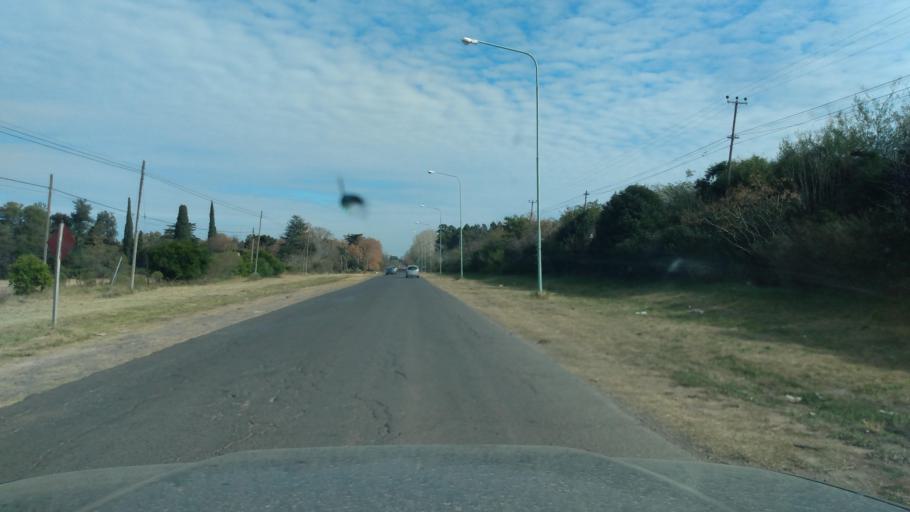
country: AR
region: Buenos Aires
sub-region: Partido de Lujan
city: Lujan
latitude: -34.5708
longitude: -59.1541
